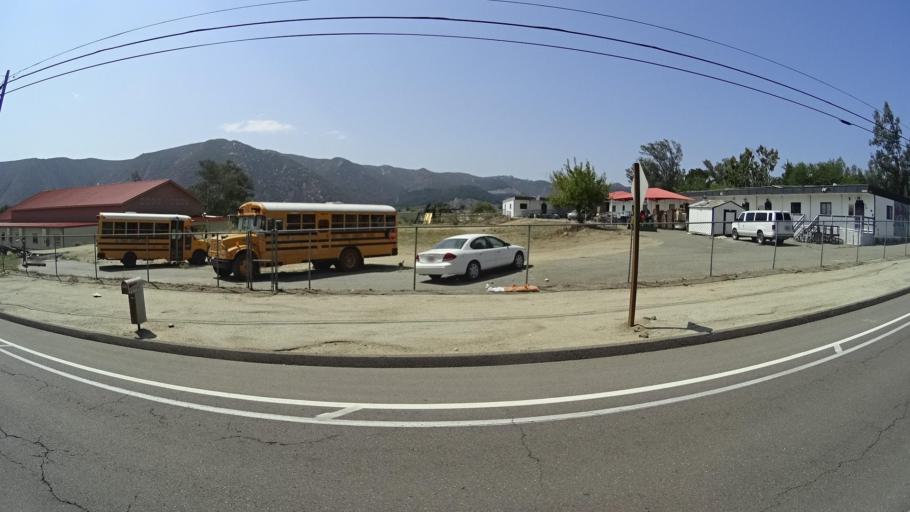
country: US
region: California
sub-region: San Diego County
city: Valley Center
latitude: 33.2784
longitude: -116.9536
